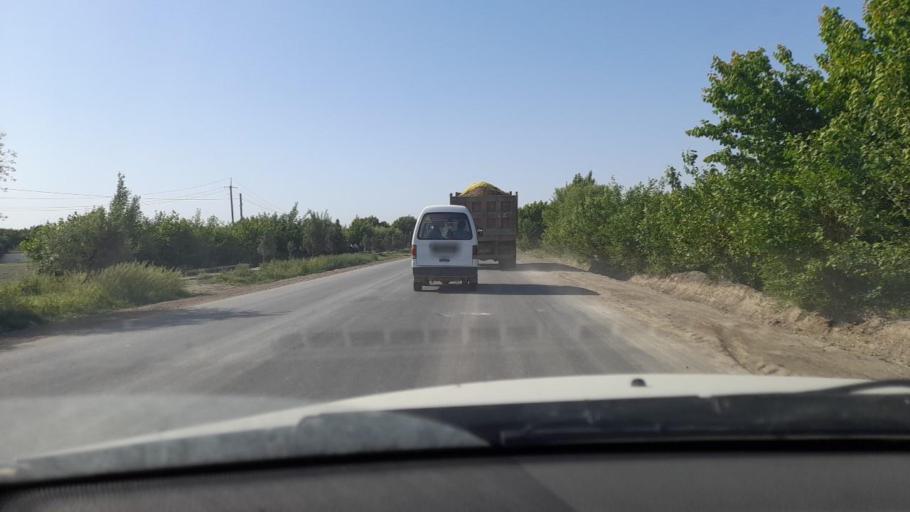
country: UZ
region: Bukhara
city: Romiton
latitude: 40.0514
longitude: 64.3283
